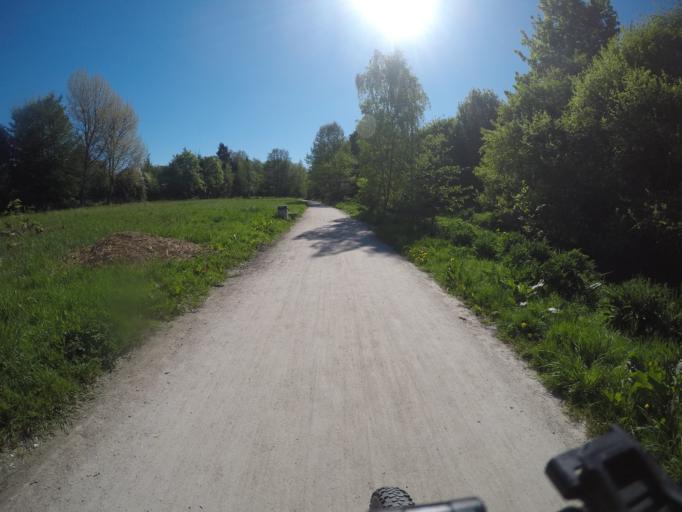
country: DE
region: Hamburg
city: Farmsen-Berne
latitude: 53.6010
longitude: 10.1238
